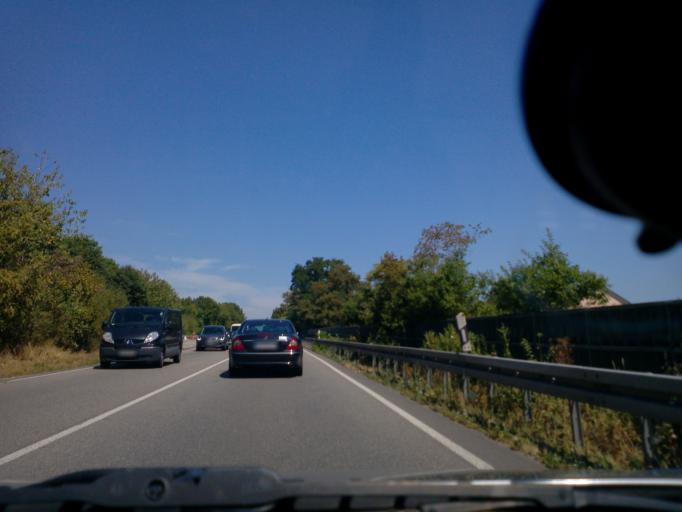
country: DE
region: Baden-Wuerttemberg
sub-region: Freiburg Region
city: Offenburg
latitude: 48.4574
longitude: 7.9314
